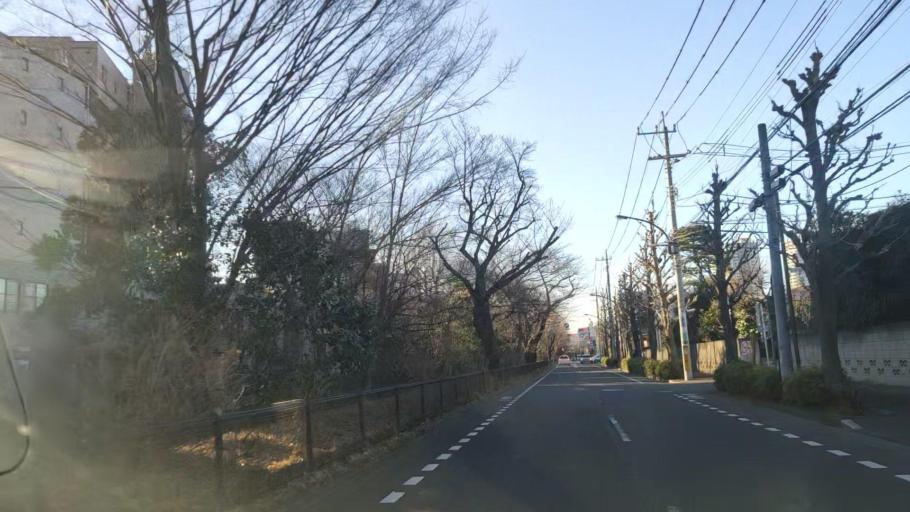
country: JP
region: Tokyo
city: Musashino
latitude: 35.7003
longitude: 139.5678
